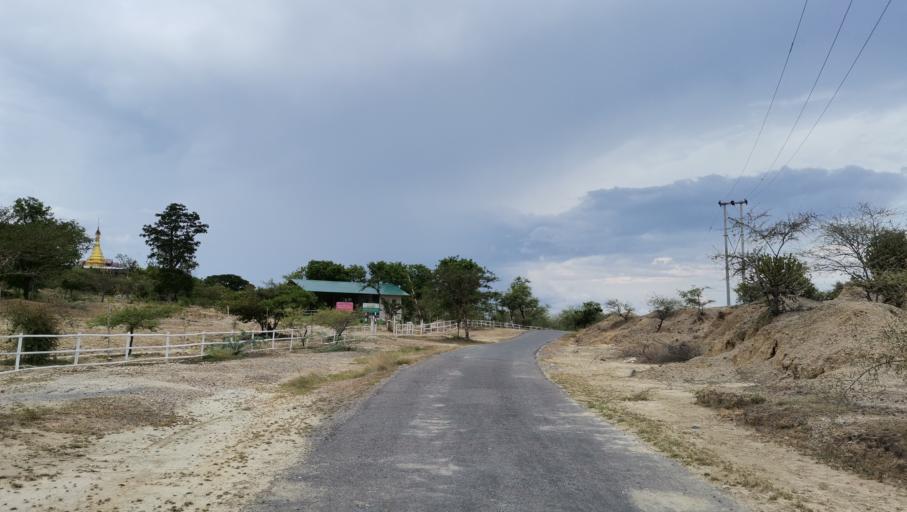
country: MM
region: Mandalay
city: Myingyan
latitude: 21.8222
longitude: 95.3962
